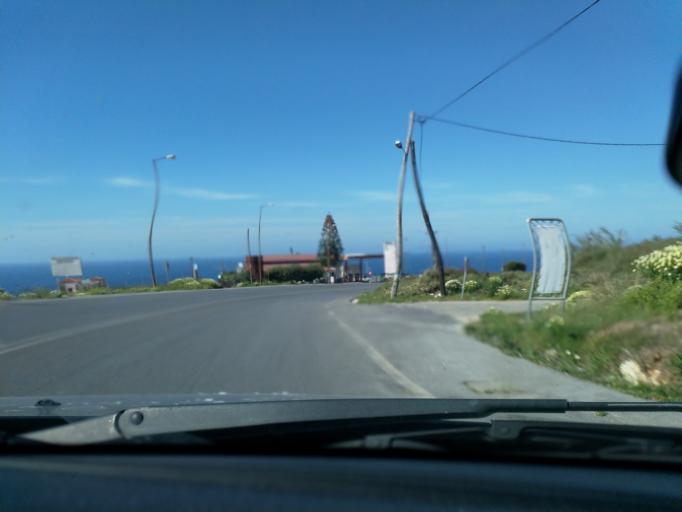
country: GR
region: Crete
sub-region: Nomos Rethymnis
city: Rethymno
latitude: 35.3539
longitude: 24.4610
